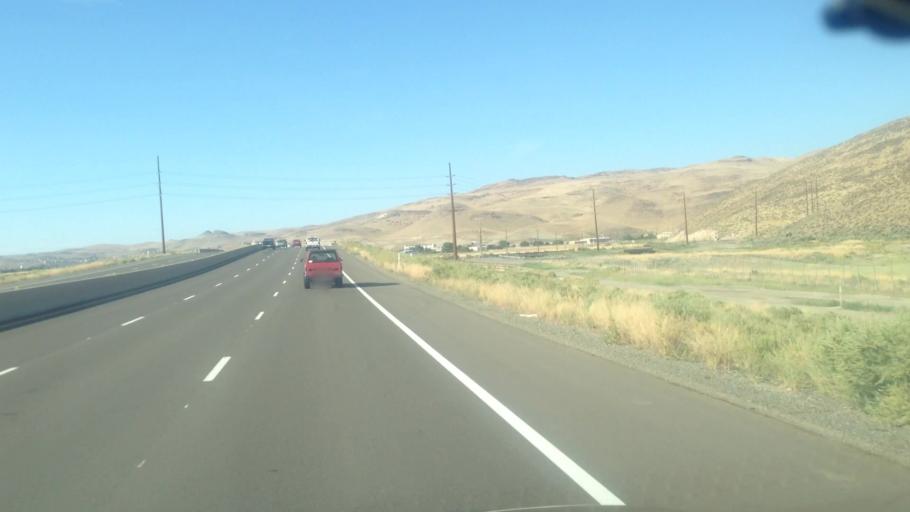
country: US
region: Nevada
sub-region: Washoe County
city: Sparks
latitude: 39.5109
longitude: -119.7146
